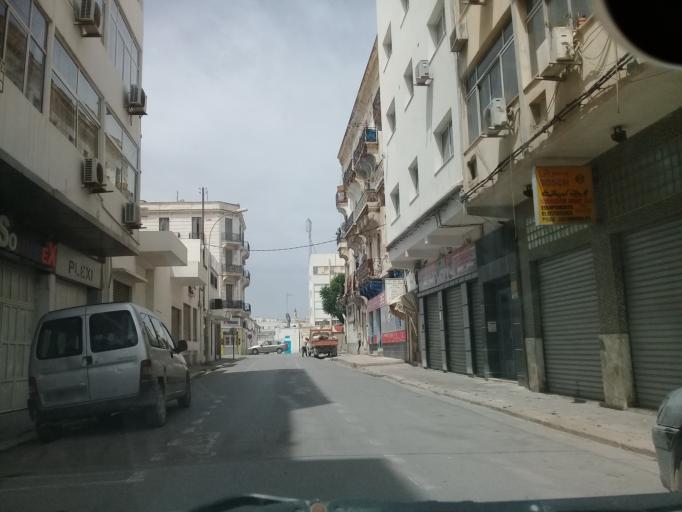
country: TN
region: Tunis
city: Tunis
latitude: 36.7944
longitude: 10.1830
